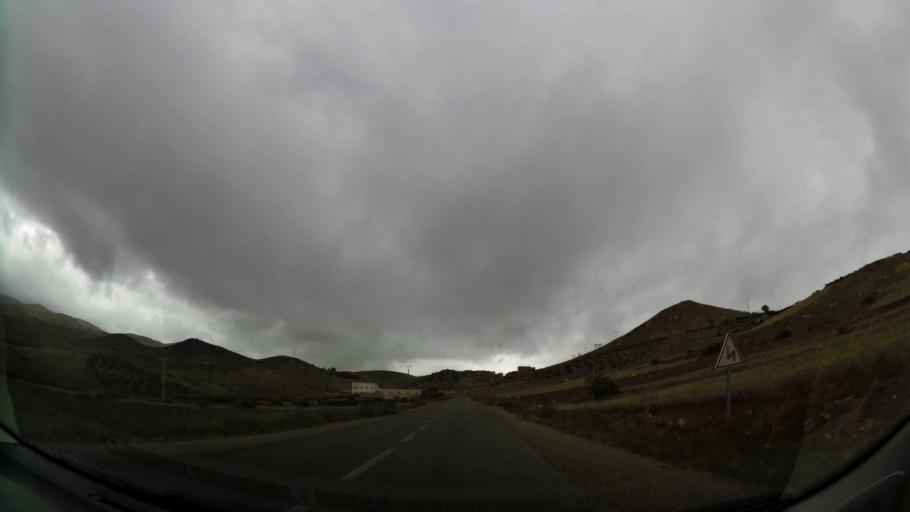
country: MA
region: Oriental
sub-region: Nador
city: Midar
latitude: 35.0620
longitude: -3.4692
